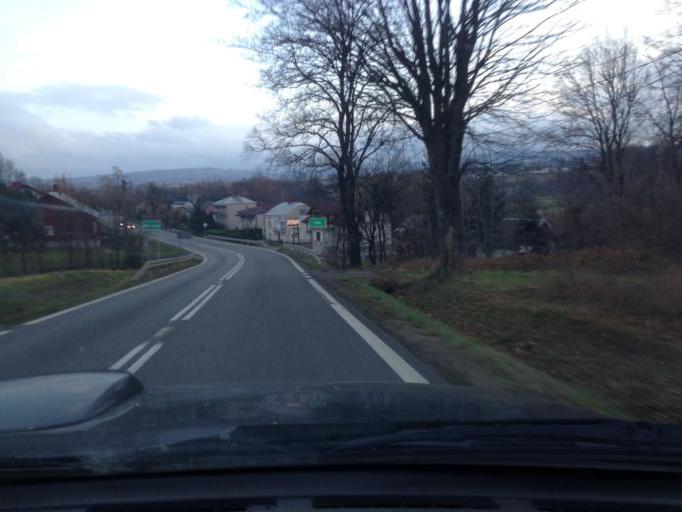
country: PL
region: Subcarpathian Voivodeship
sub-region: Powiat jasielski
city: Nowy Zmigrod
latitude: 49.6248
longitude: 21.5356
